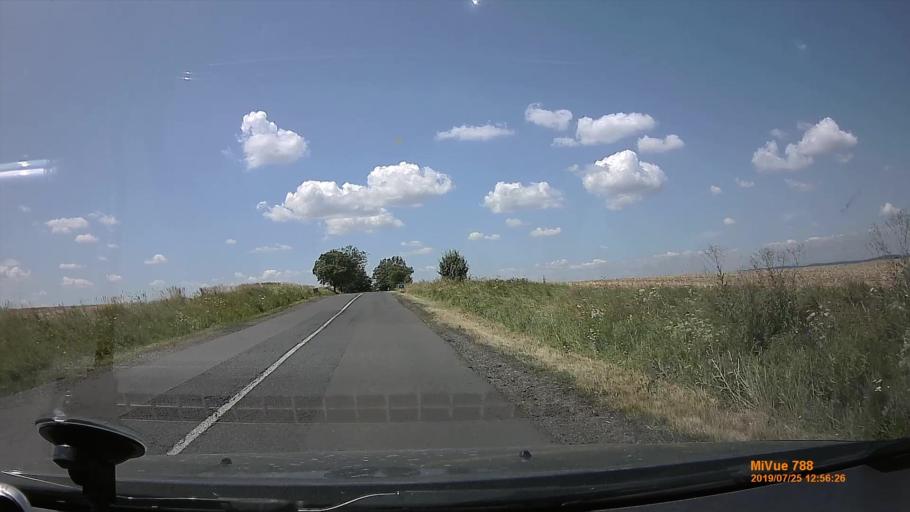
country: HU
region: Borsod-Abauj-Zemplen
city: Abaujszanto
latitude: 48.3134
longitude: 21.1709
